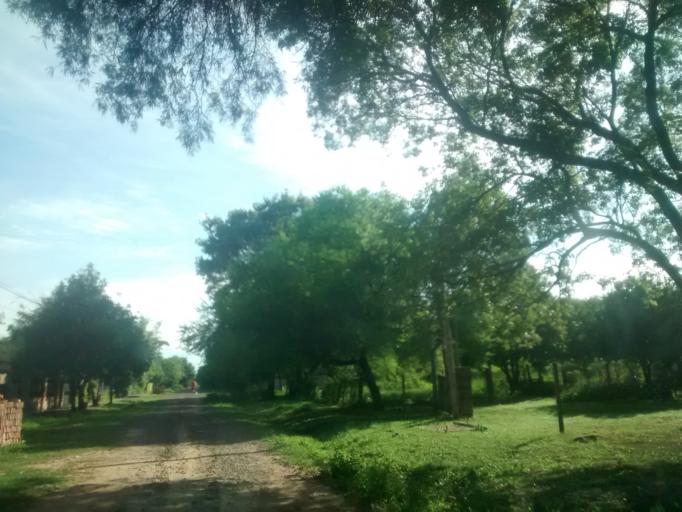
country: AR
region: Chaco
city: Puerto Tirol
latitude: -27.3773
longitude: -59.0954
